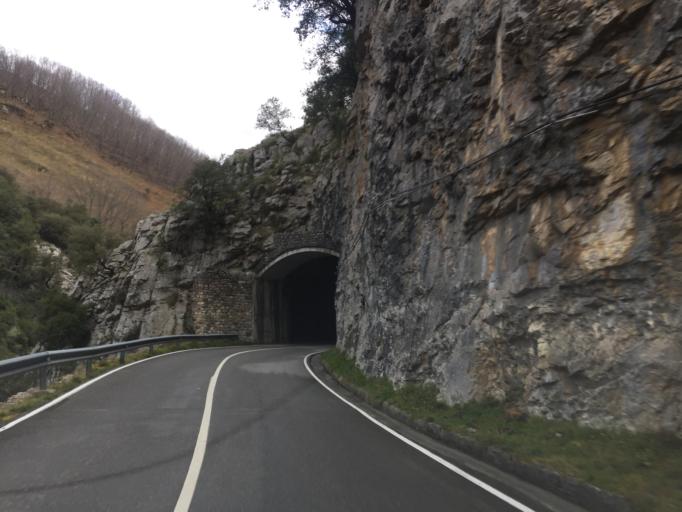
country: ES
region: Asturias
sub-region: Province of Asturias
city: Carrena
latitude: 43.2900
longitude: -4.8256
